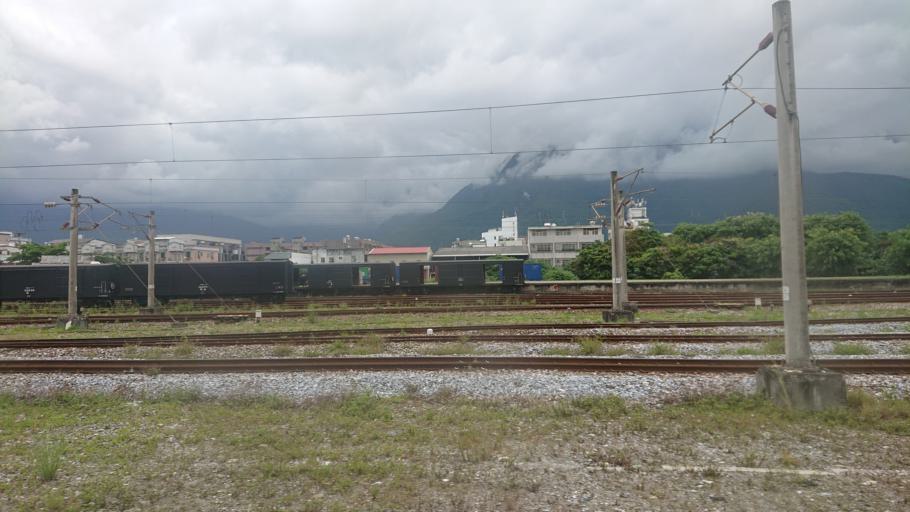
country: TW
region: Taiwan
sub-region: Hualien
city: Hualian
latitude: 23.9971
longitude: 121.6030
